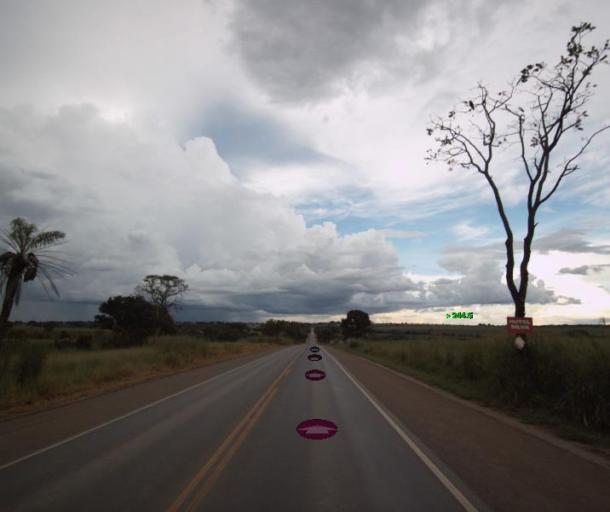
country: BR
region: Goias
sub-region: Itapaci
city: Itapaci
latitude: -14.8778
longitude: -49.3352
